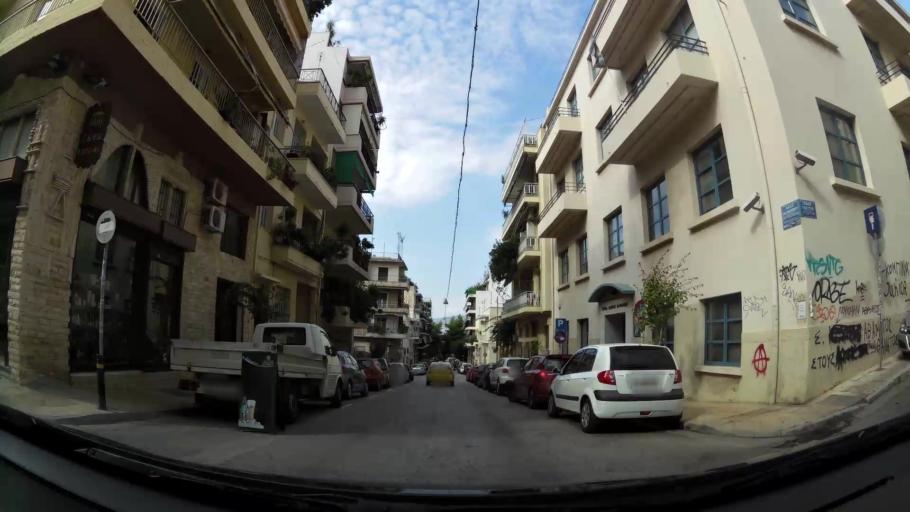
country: GR
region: Attica
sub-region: Nomarchia Athinas
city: Athens
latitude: 37.9764
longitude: 23.7167
